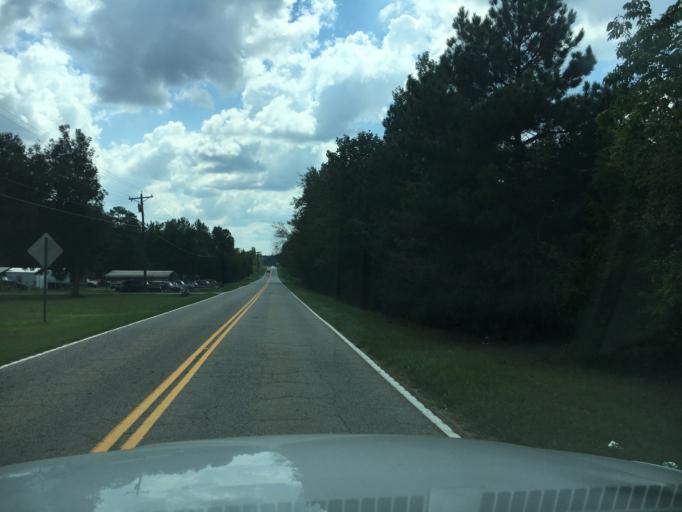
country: US
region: South Carolina
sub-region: Greenwood County
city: Greenwood
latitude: 34.1293
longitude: -82.1263
